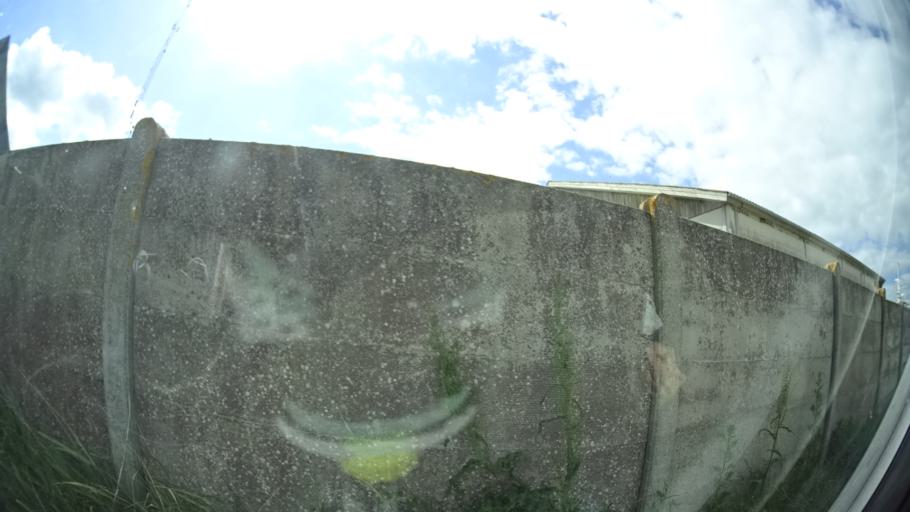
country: DK
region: Central Jutland
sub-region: Norddjurs Kommune
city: Grenaa
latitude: 56.5323
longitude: 10.7149
